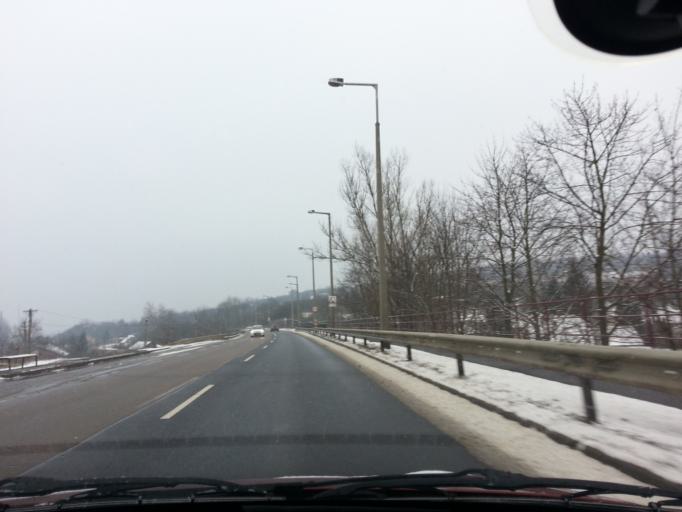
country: HU
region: Nograd
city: Salgotarjan
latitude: 48.0860
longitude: 19.7875
